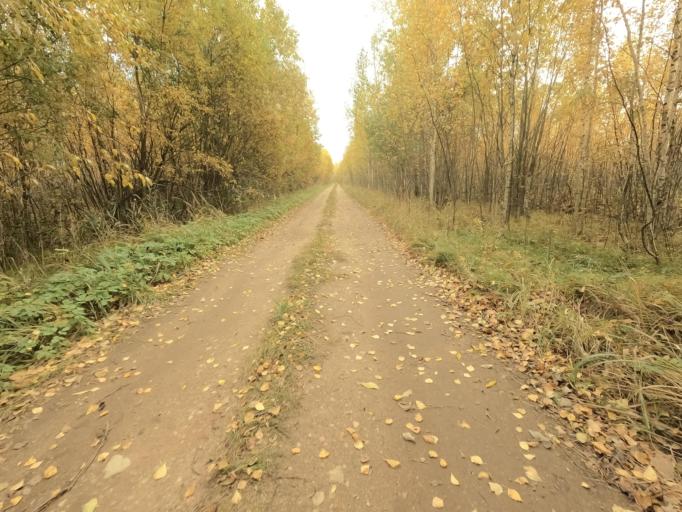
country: RU
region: Novgorod
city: Pankovka
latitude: 58.8753
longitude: 30.8764
